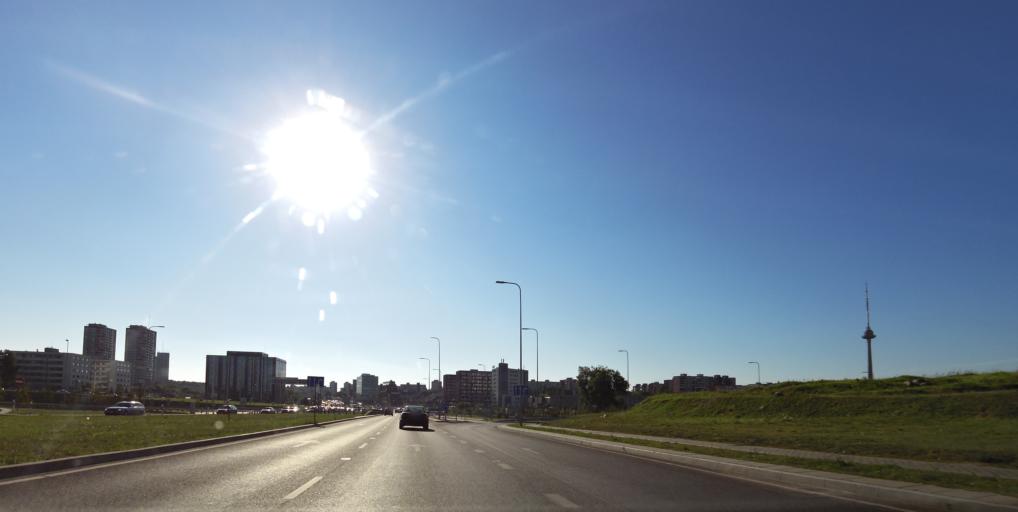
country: LT
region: Vilnius County
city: Justiniskes
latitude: 54.7009
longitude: 25.2059
